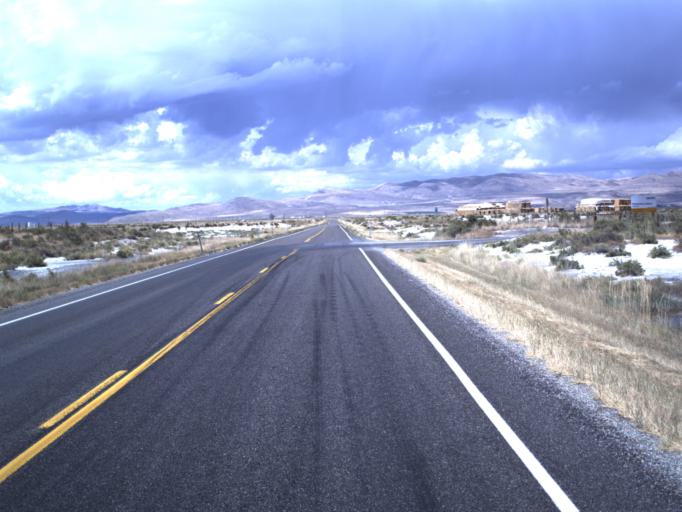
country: US
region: Utah
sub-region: Box Elder County
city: Tremonton
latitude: 41.5824
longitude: -112.2581
